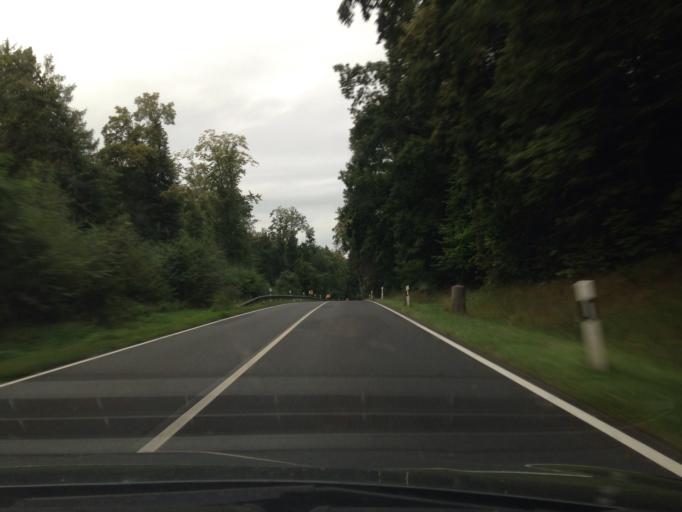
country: DE
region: Mecklenburg-Vorpommern
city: Carpin
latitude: 53.3661
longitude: 13.1883
